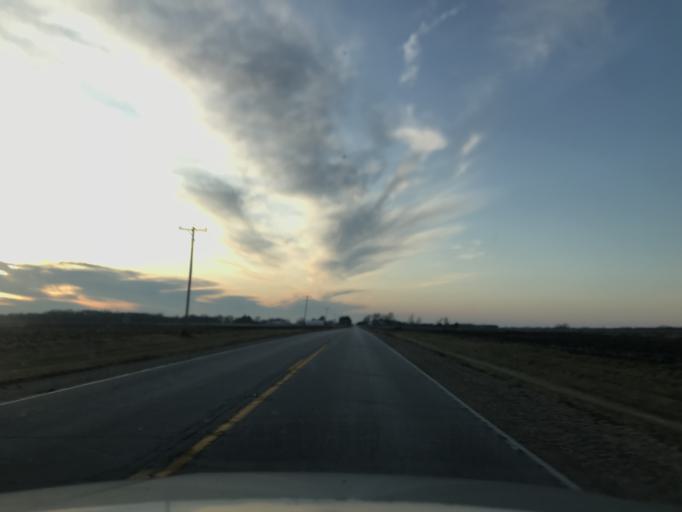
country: US
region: Illinois
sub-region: Warren County
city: Monmouth
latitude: 41.0248
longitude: -90.7588
